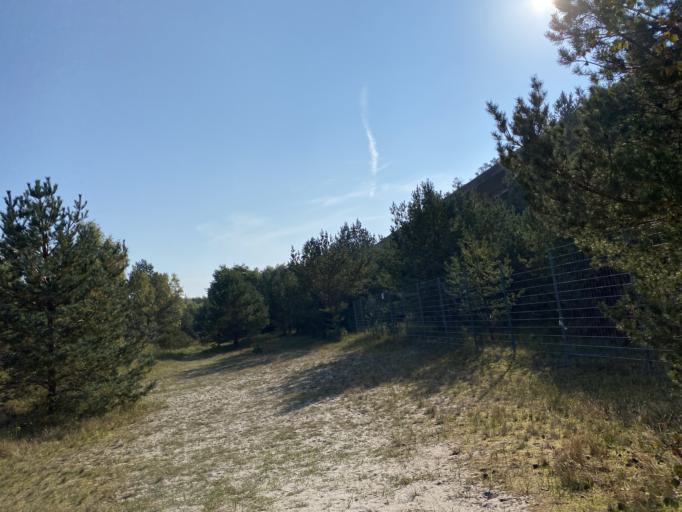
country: DE
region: Mecklenburg-Vorpommern
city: Sagard
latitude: 54.4582
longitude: 13.5683
